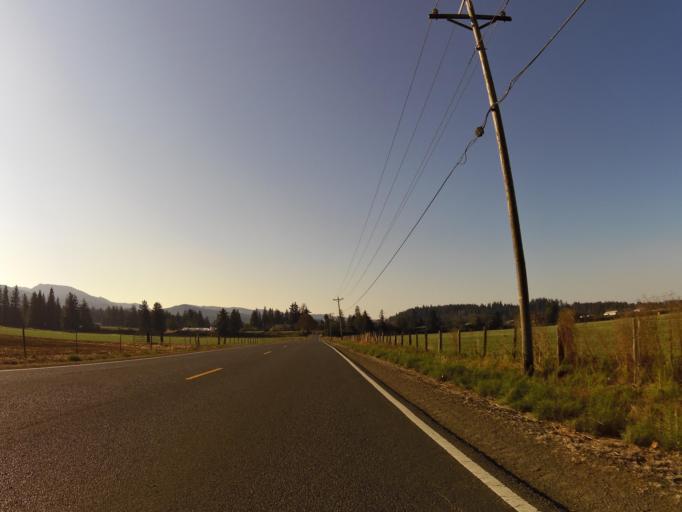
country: US
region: Oregon
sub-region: Tillamook County
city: Tillamook
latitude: 45.4359
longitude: -123.7776
